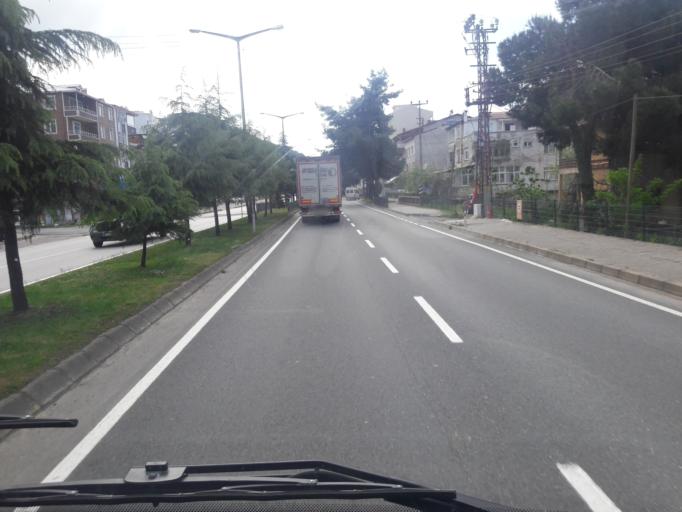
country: TR
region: Ordu
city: Gulyali
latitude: 40.9656
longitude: 38.0689
